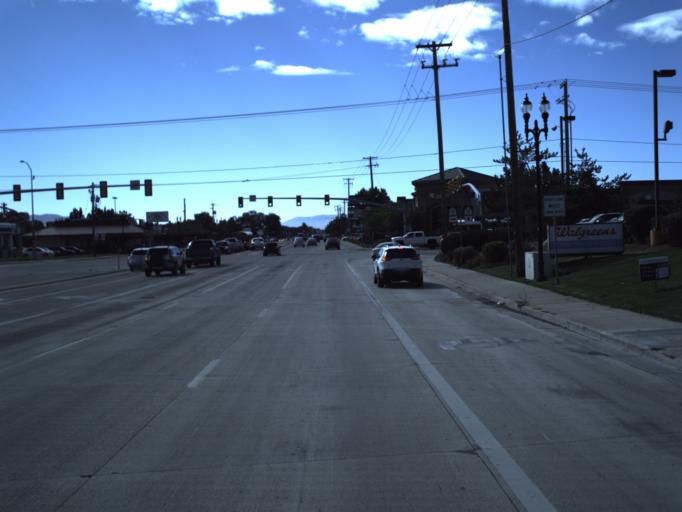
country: US
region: Utah
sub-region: Salt Lake County
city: West Jordan
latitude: 40.6103
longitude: -111.9389
